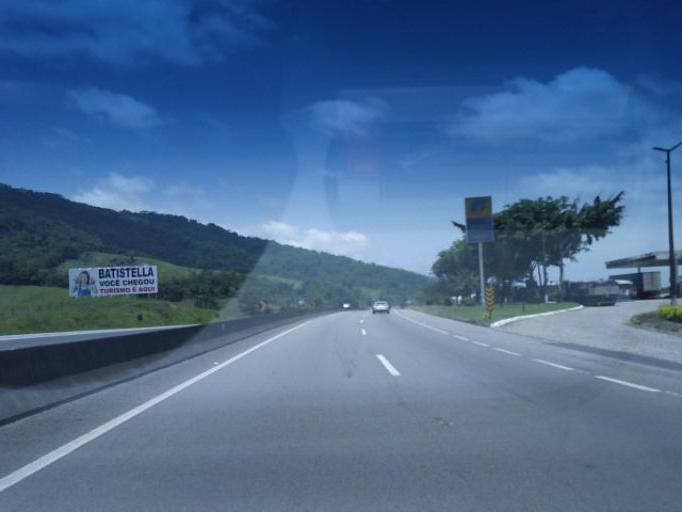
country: BR
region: Sao Paulo
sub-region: Miracatu
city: Miracatu
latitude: -24.3026
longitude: -47.4867
